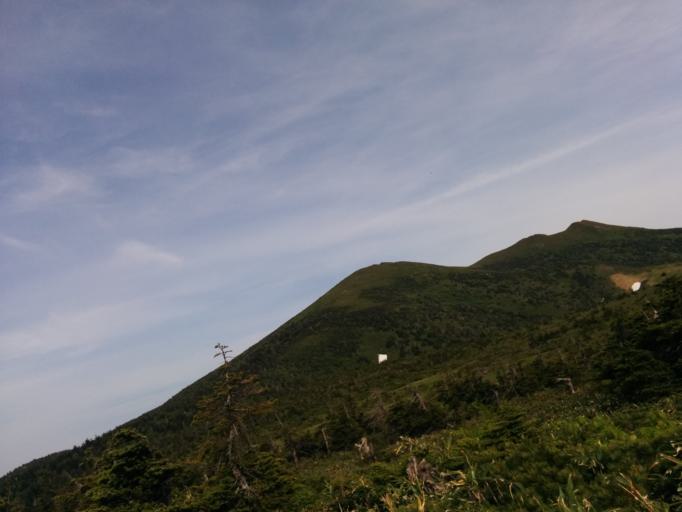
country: JP
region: Aomori
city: Aomori Shi
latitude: 40.6749
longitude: 140.8639
